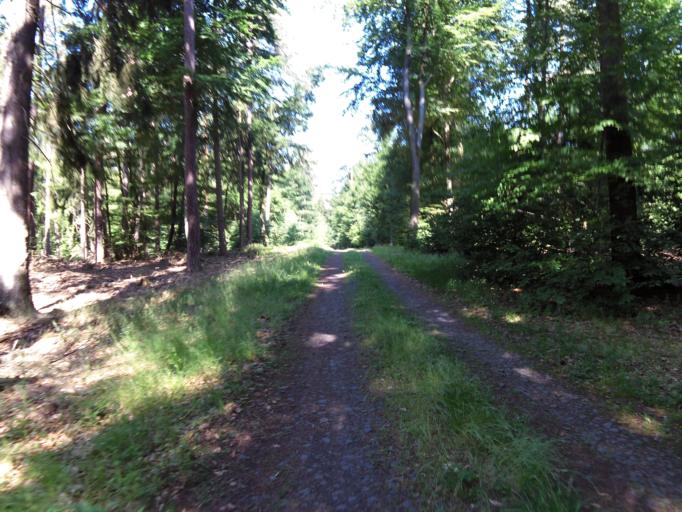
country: DE
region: Rheinland-Pfalz
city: Weidenthal
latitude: 49.4432
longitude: 8.0104
